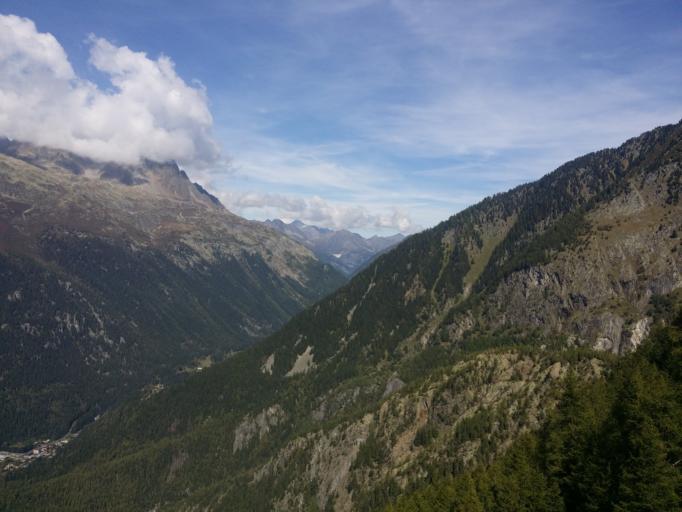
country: FR
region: Rhone-Alpes
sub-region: Departement de la Haute-Savoie
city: Chamonix-Mont-Blanc
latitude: 45.9338
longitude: 6.9107
